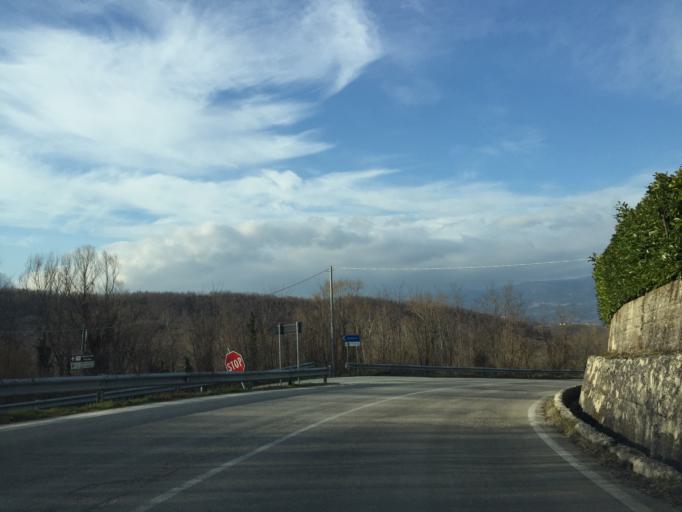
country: IT
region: Molise
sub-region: Provincia di Campobasso
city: San Massimo
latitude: 41.4855
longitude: 14.4042
